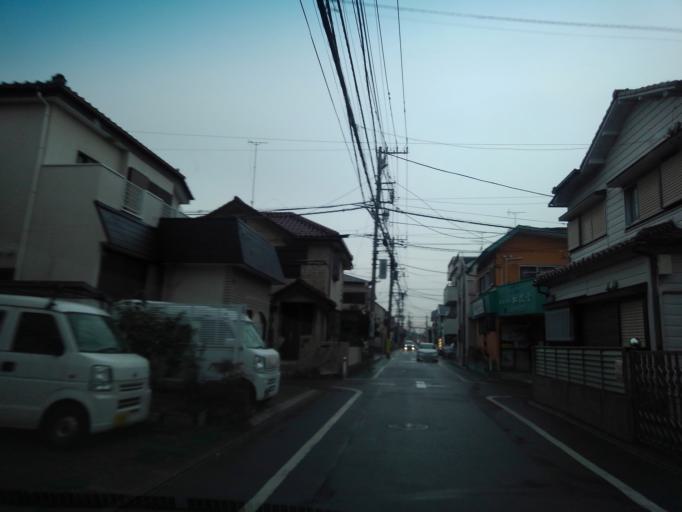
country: JP
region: Tokyo
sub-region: Machida-shi
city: Machida
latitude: 35.5134
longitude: 139.4419
